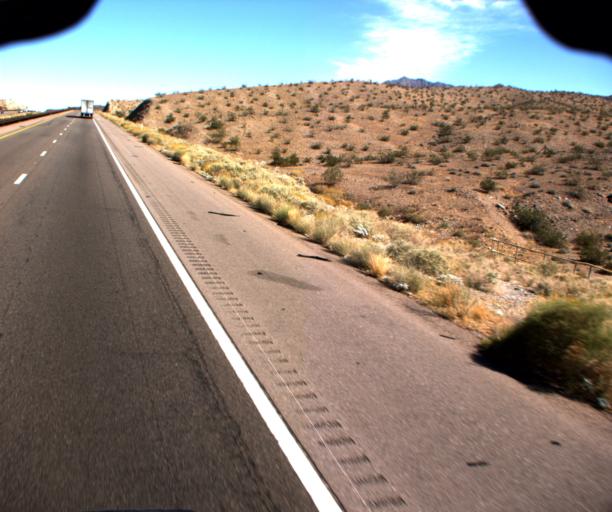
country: US
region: Nevada
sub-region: Clark County
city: Boulder City
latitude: 35.9217
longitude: -114.6316
